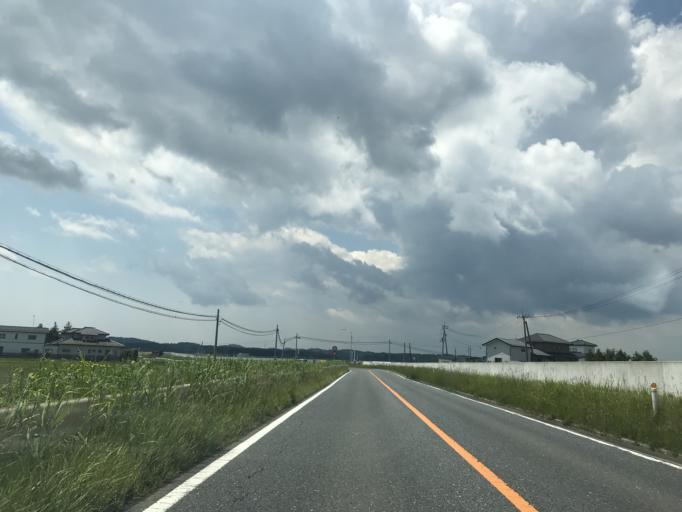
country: JP
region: Miyagi
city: Matsushima
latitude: 38.4508
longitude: 141.0819
